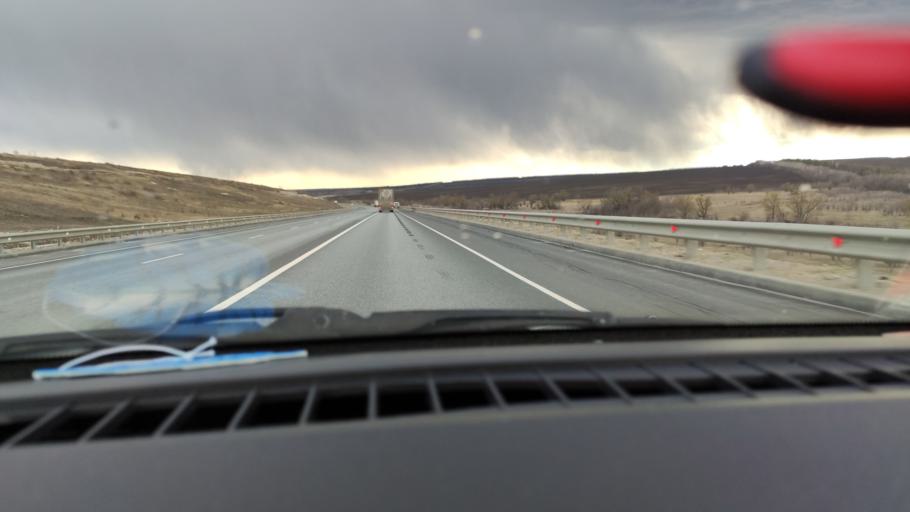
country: RU
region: Saratov
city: Yelshanka
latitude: 51.8719
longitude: 46.5046
